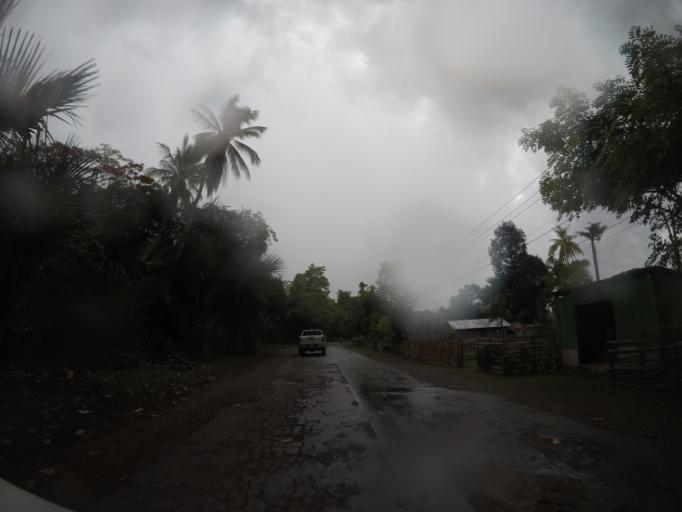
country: ID
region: East Nusa Tenggara
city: Atambua
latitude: -8.9582
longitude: 124.9840
